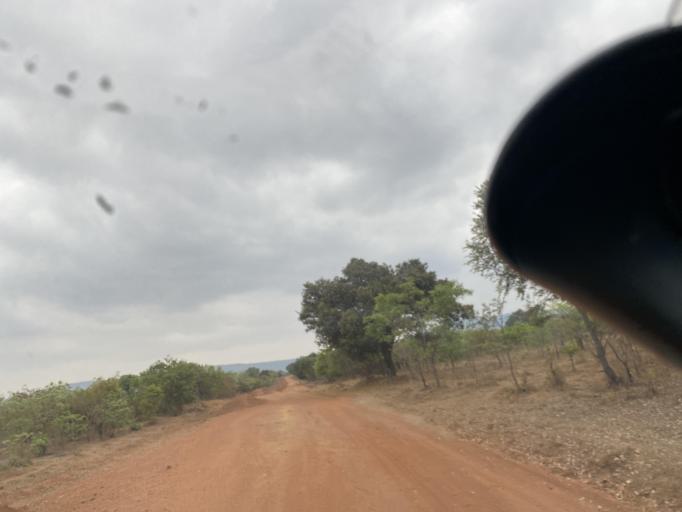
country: ZM
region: Lusaka
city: Chongwe
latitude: -15.2195
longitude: 28.7535
